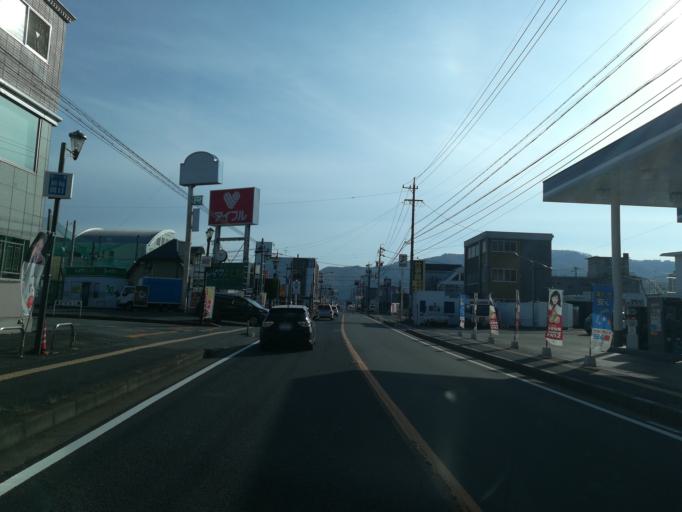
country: JP
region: Nagano
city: Ueda
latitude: 36.3953
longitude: 138.2660
